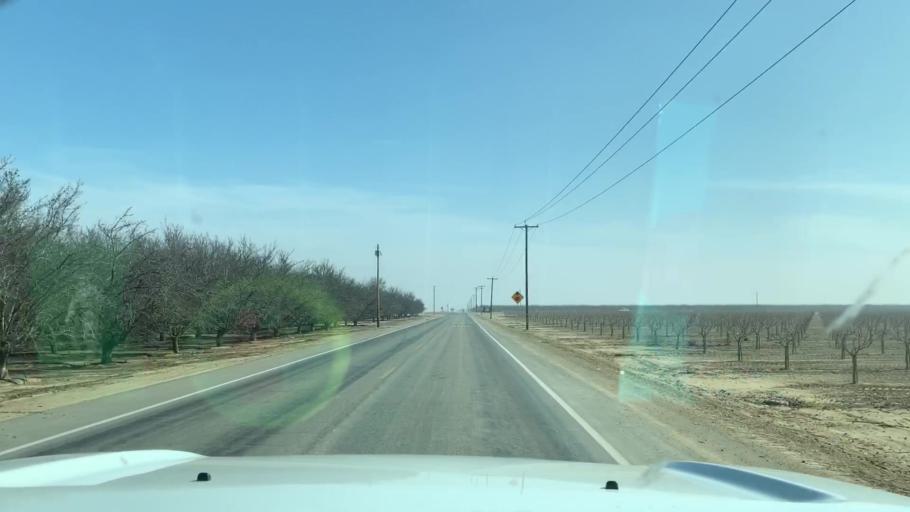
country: US
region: California
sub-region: Kern County
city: Buttonwillow
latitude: 35.4424
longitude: -119.4778
